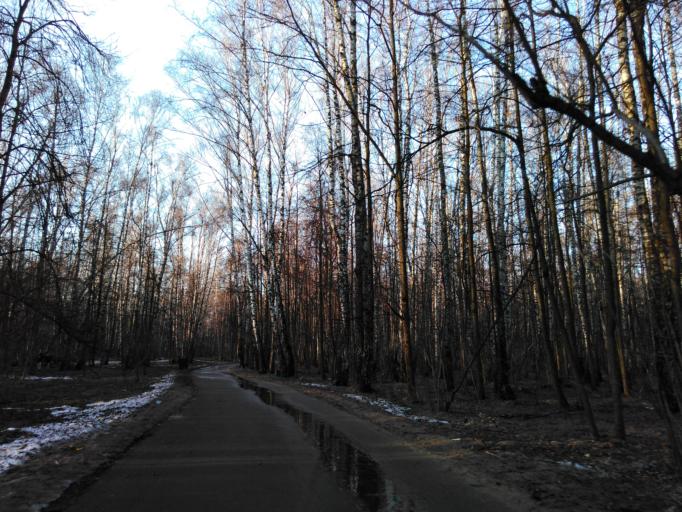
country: RU
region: Moscow
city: Zyuzino
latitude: 55.6420
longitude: 37.5666
